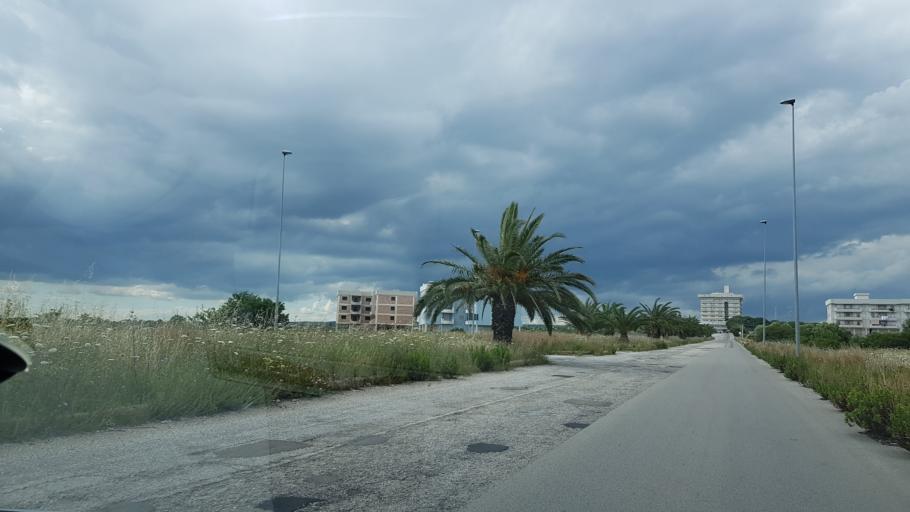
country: IT
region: Apulia
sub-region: Provincia di Taranto
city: Paolo VI
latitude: 40.5328
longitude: 17.2770
